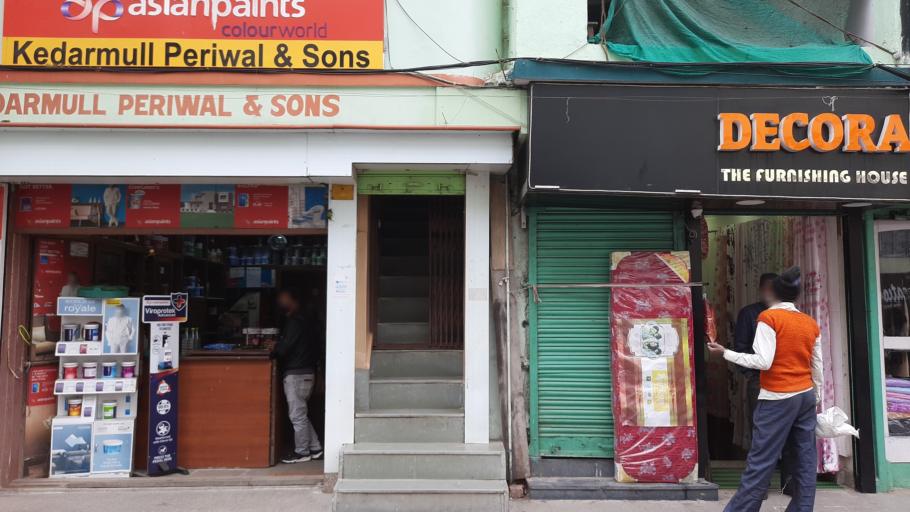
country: IN
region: Sikkim
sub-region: East District
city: Gangtok
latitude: 27.3297
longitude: 88.6126
